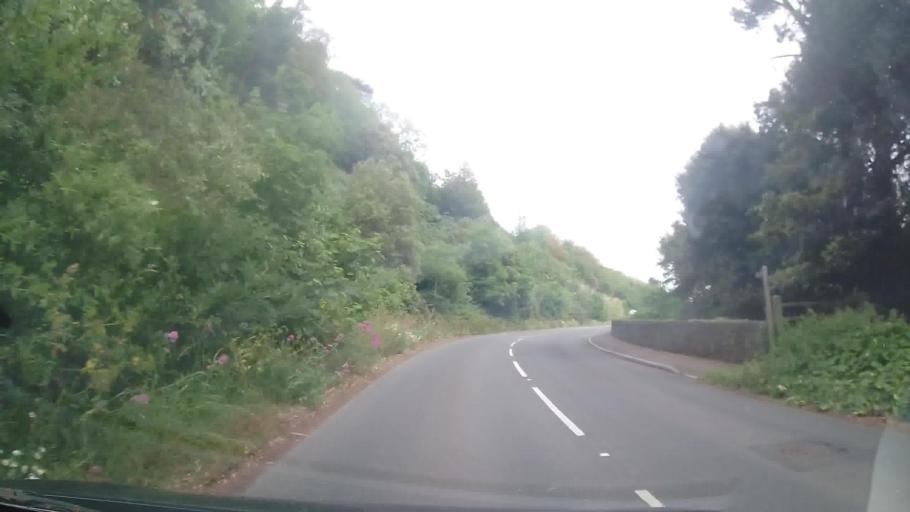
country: GB
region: England
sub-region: Devon
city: Dartmouth
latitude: 50.3209
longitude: -3.6066
